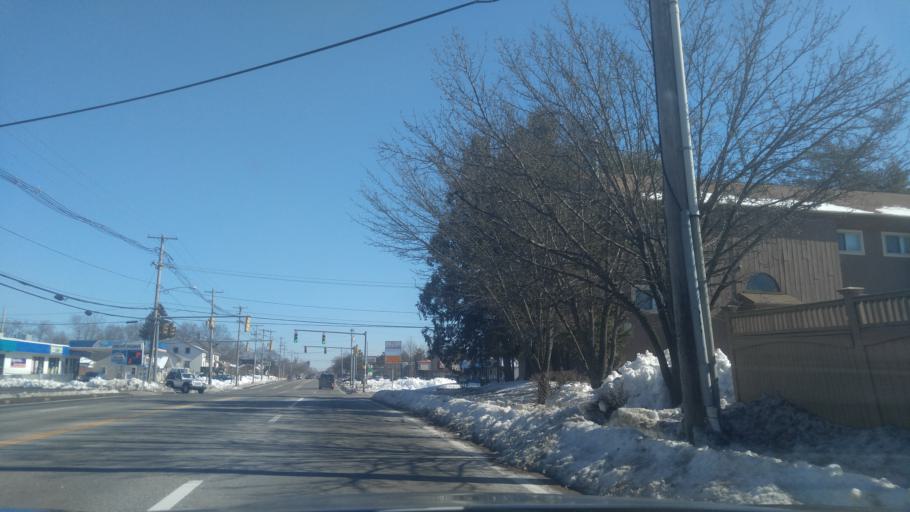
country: US
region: Rhode Island
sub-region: Providence County
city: Cranston
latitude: 41.7514
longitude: -71.4175
